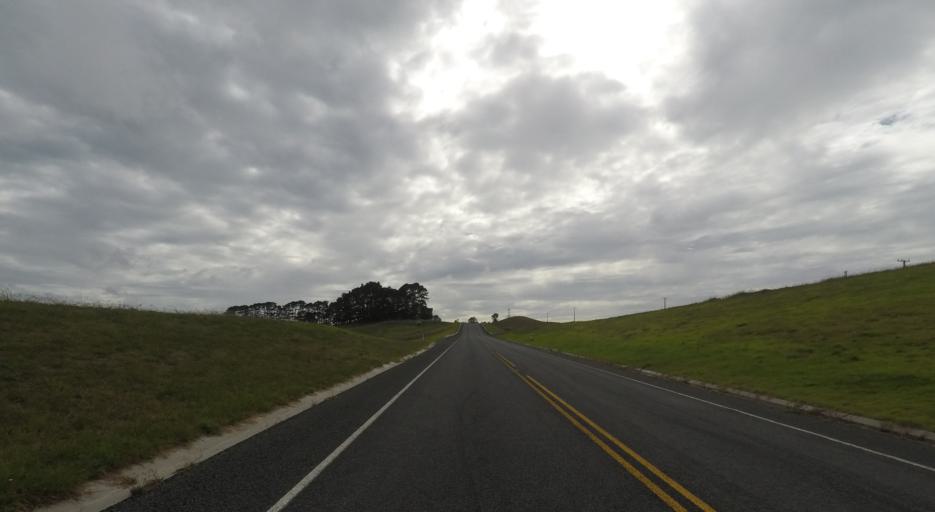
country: NZ
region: Auckland
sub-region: Auckland
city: Rothesay Bay
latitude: -36.6585
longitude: 174.6840
